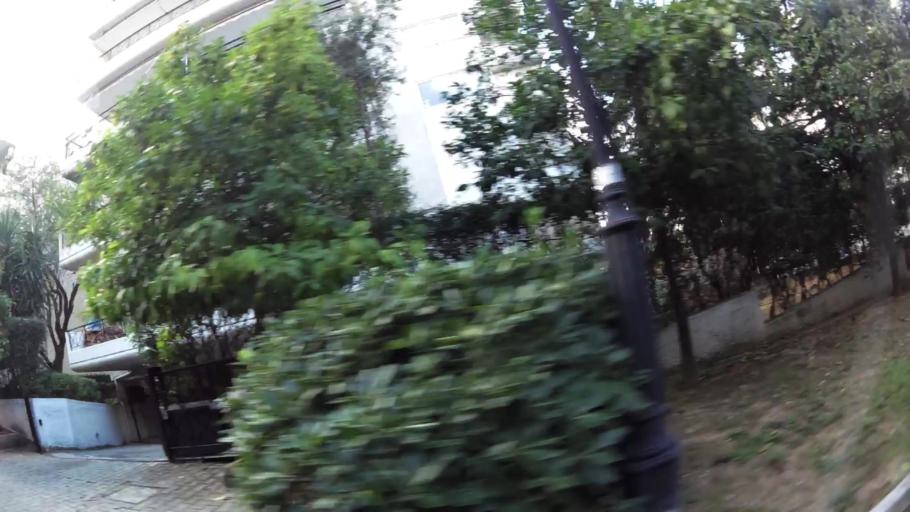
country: GR
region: Attica
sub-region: Nomarchia Athinas
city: Melissia
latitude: 38.0541
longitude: 23.8187
